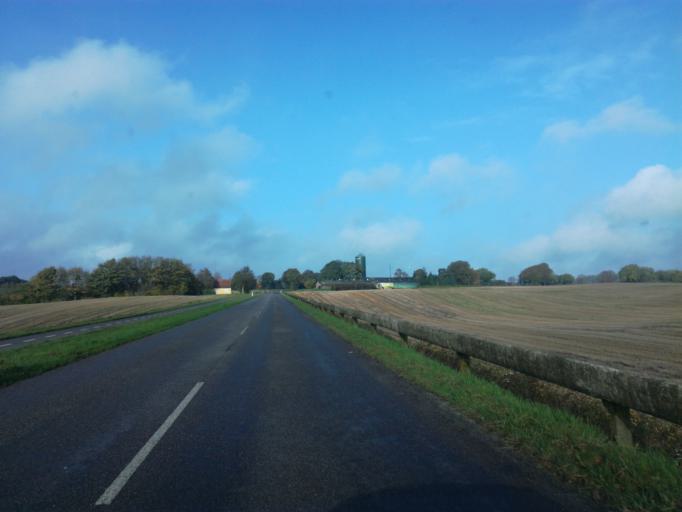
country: DK
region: South Denmark
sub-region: Vejle Kommune
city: Borkop
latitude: 55.6558
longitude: 9.6383
